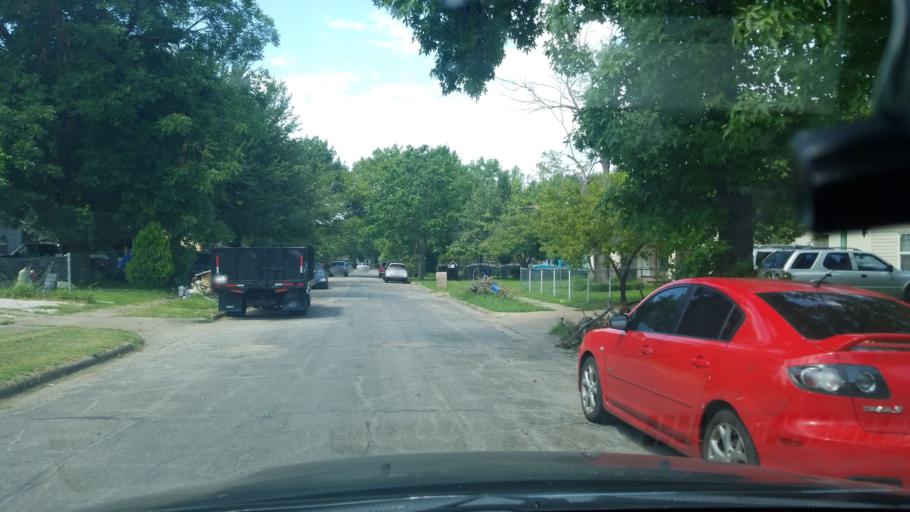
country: US
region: Texas
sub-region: Dallas County
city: Balch Springs
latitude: 32.7369
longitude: -96.6898
